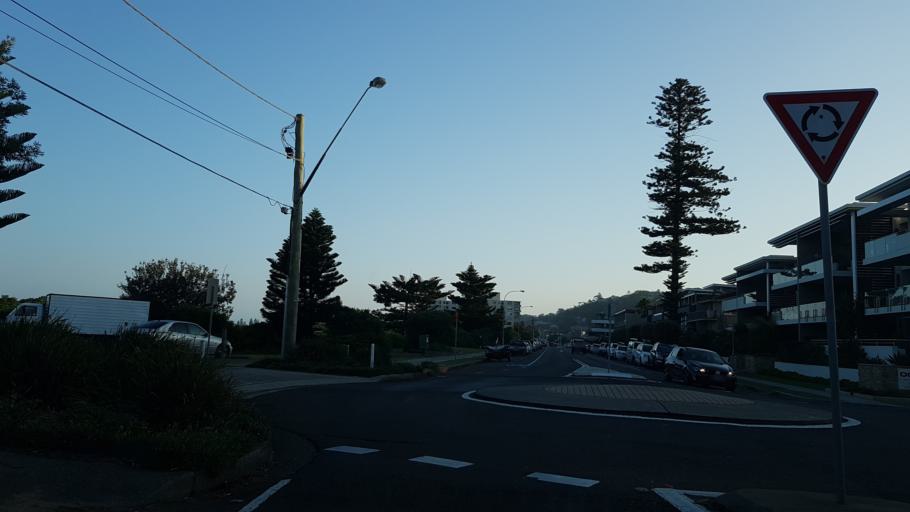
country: AU
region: New South Wales
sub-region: Warringah
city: Narrabeen
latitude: -33.7168
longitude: 151.2990
